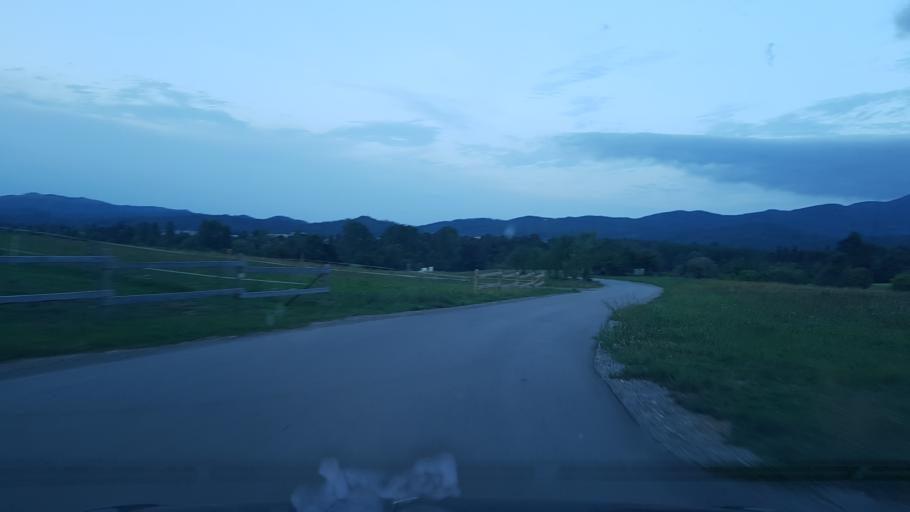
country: SI
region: Postojna
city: Postojna
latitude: 45.7522
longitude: 14.1796
